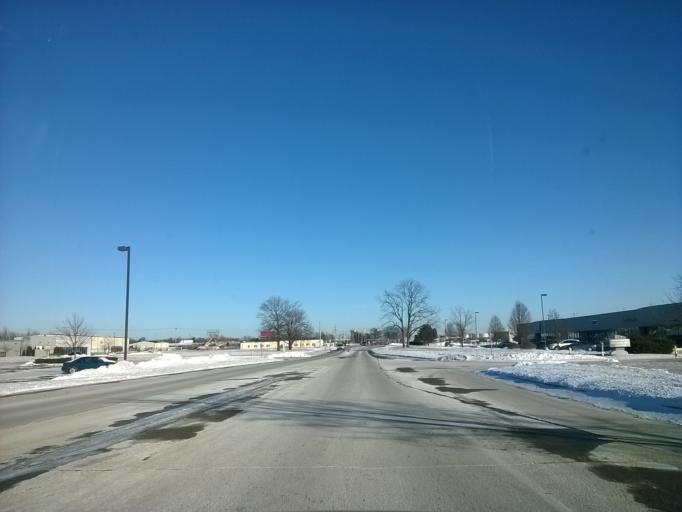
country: US
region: Indiana
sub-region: Boone County
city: Zionsville
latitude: 39.9251
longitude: -86.2627
